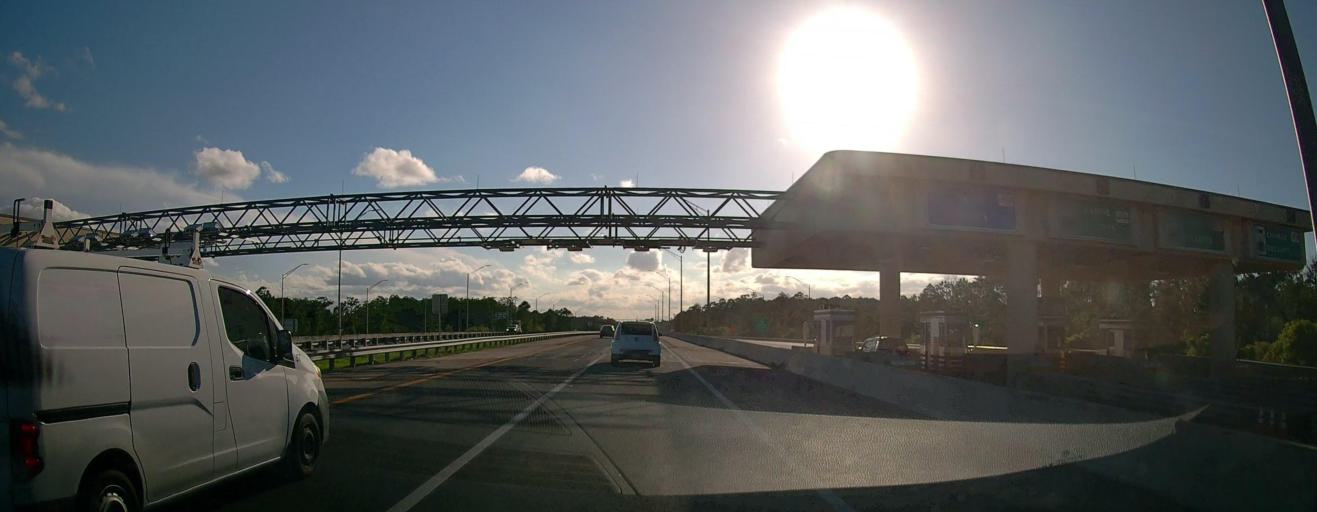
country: US
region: Florida
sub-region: Orange County
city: Alafaya
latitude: 28.4517
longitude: -81.2087
